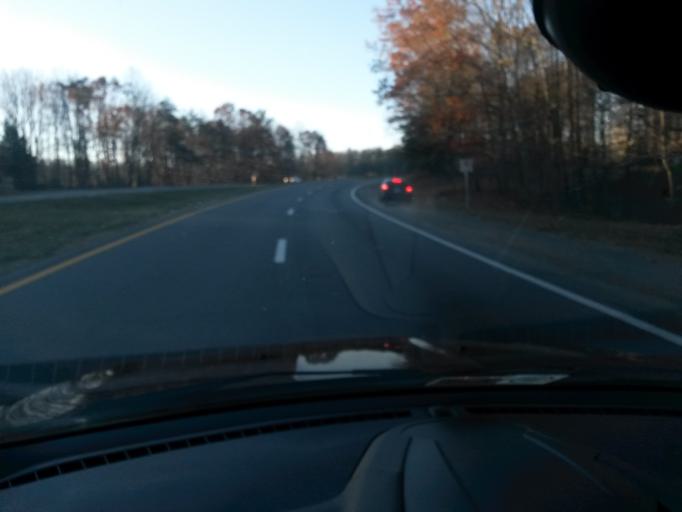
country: US
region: Virginia
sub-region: Franklin County
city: Henry Fork
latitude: 36.8551
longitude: -79.8764
